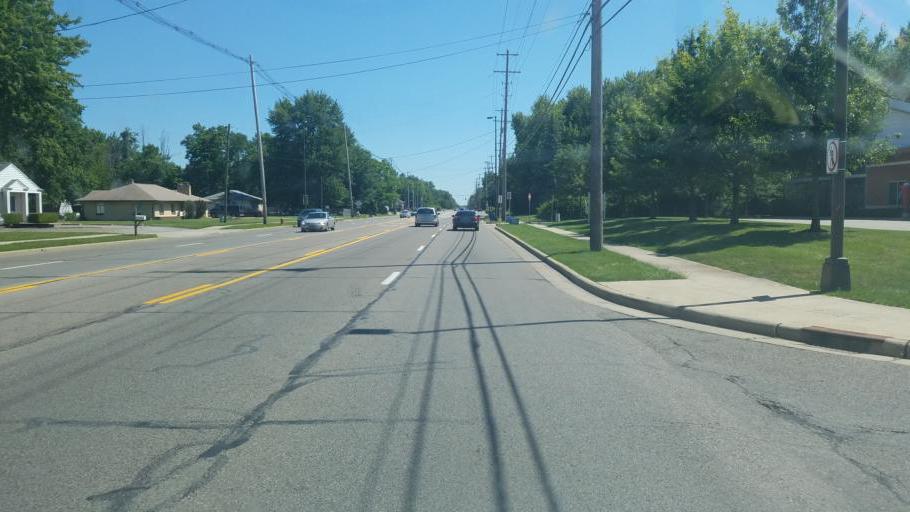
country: US
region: Ohio
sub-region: Franklin County
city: Gahanna
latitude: 40.0233
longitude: -82.9112
